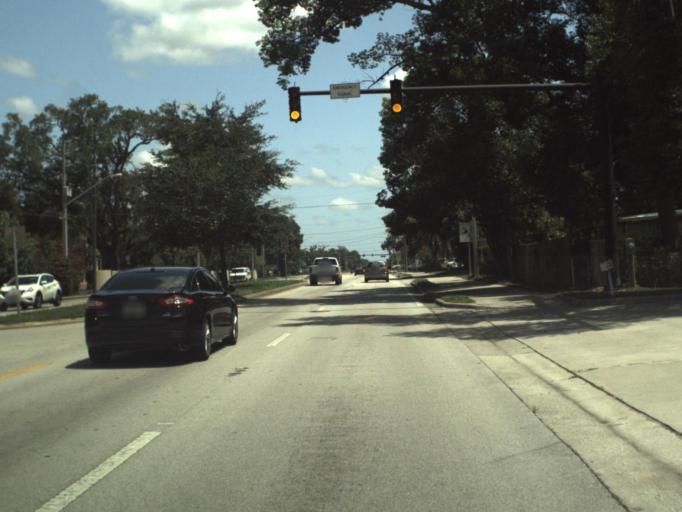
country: US
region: Florida
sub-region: Orange County
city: Conway
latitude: 28.4992
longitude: -81.3308
